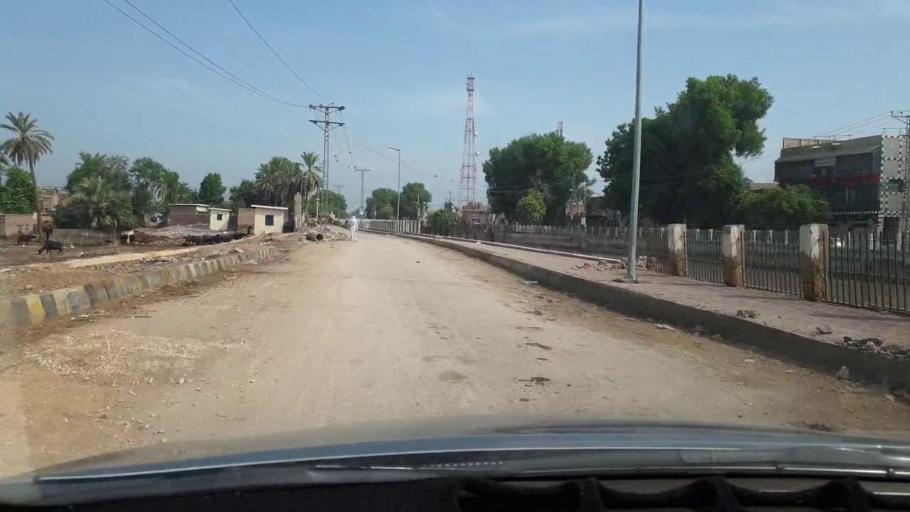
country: PK
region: Sindh
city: Khairpur
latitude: 27.5237
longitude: 68.7555
